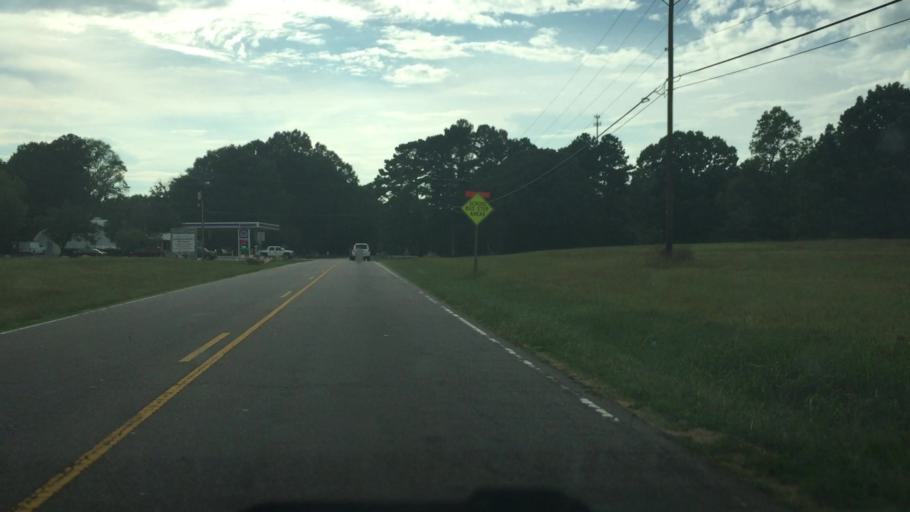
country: US
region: North Carolina
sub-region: Gaston County
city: Davidson
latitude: 35.4898
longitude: -80.7634
